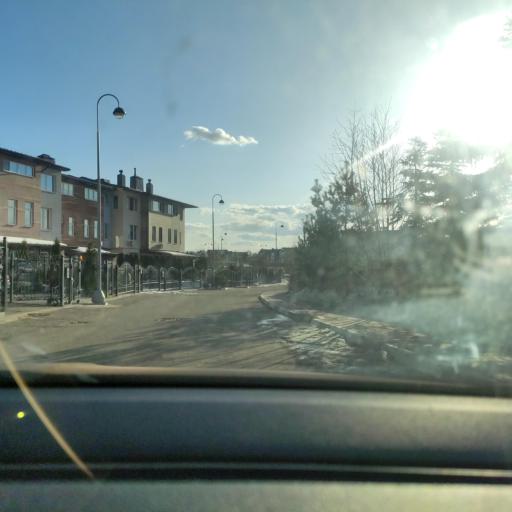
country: RU
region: Moscow
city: Khimki
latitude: 55.9063
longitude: 37.3831
